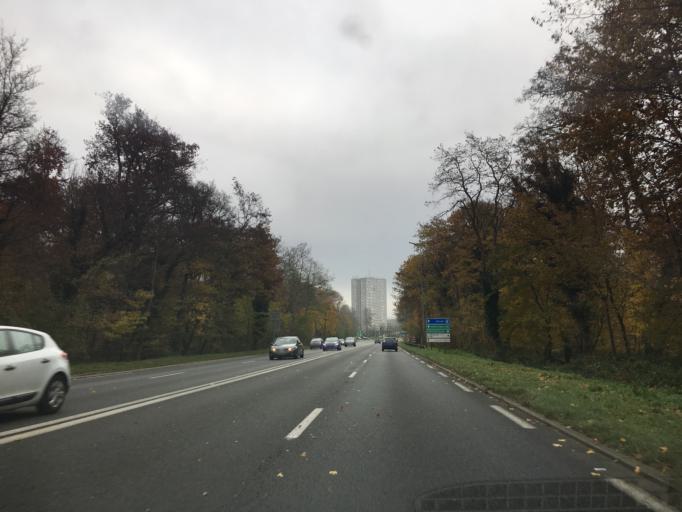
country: FR
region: Ile-de-France
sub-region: Departement de Seine-et-Marne
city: Fontainebleau
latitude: 48.4110
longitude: 2.6826
